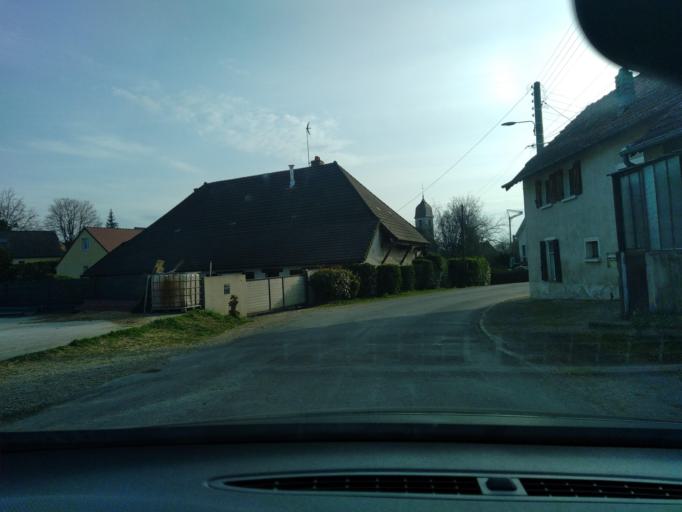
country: FR
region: Franche-Comte
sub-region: Departement du Jura
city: Chaussin
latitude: 46.9890
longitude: 5.4634
